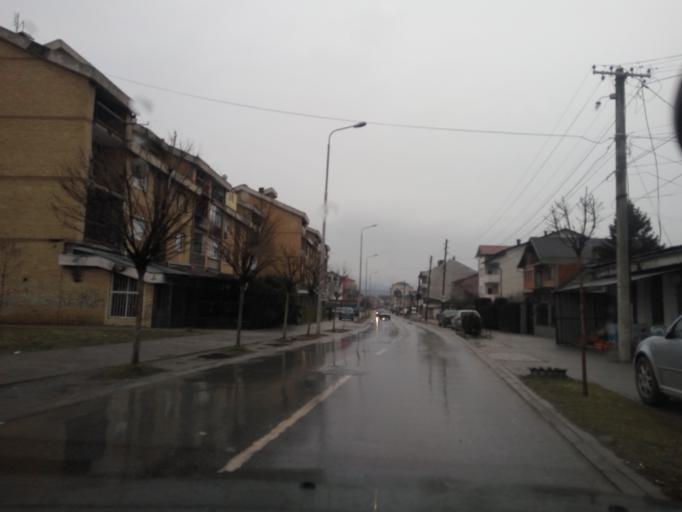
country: XK
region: Gjakova
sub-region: Komuna e Gjakoves
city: Gjakove
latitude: 42.3745
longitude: 20.4406
